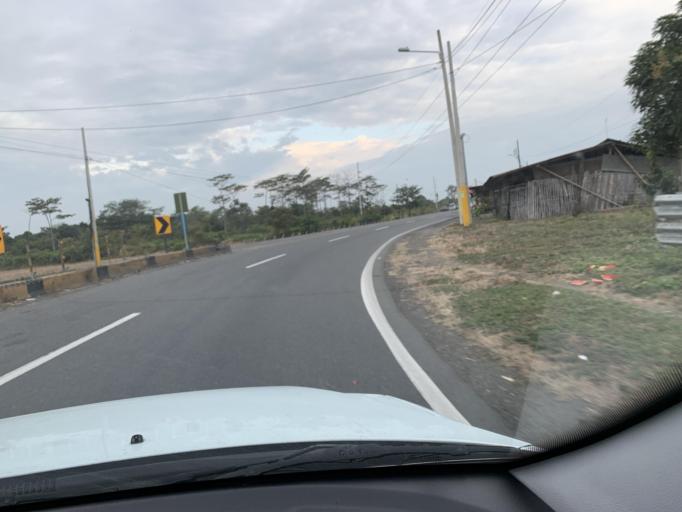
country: EC
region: Guayas
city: Yaguachi Nuevo
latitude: -2.2360
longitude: -79.6393
